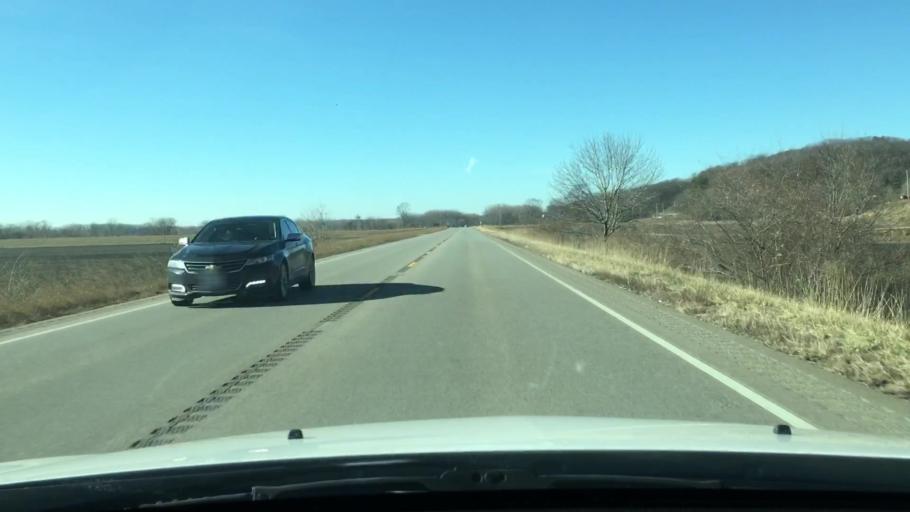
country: US
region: Illinois
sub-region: Peoria County
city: Glasford
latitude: 40.5522
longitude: -89.7987
